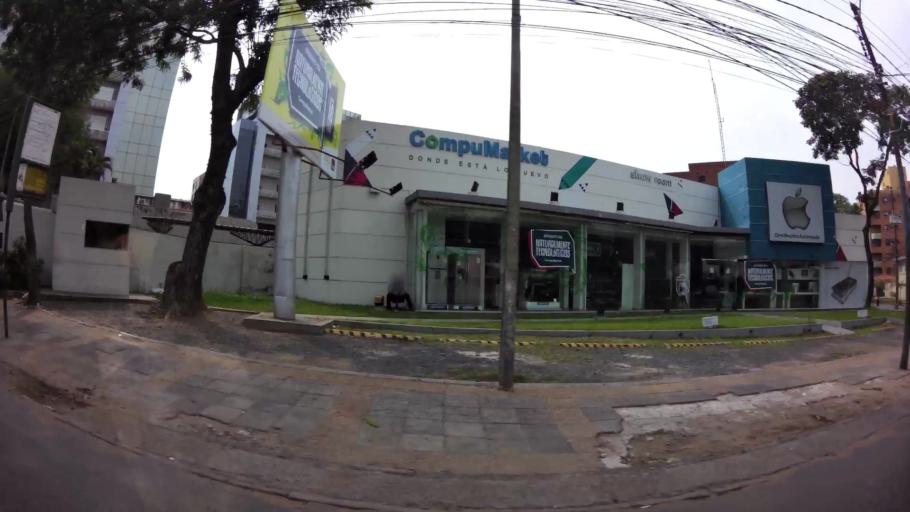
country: PY
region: Asuncion
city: Asuncion
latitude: -25.2856
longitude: -57.5700
